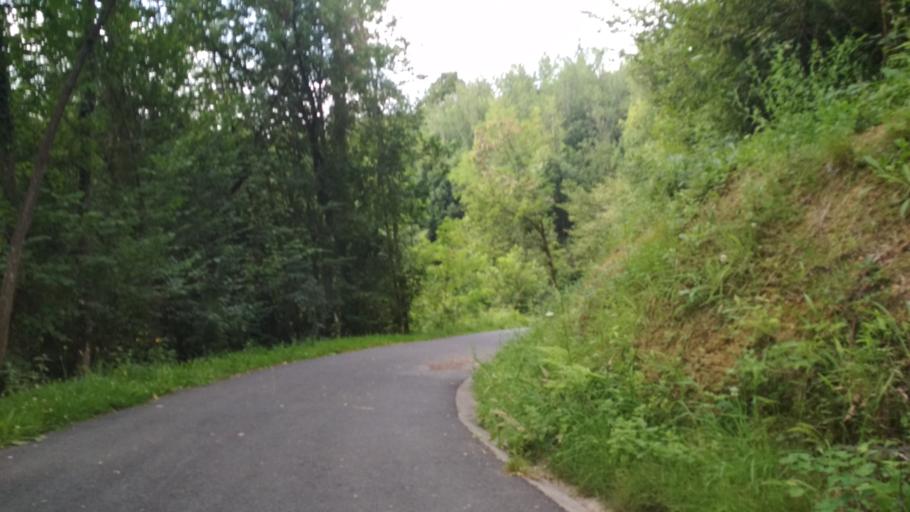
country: ES
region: Basque Country
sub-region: Provincia de Guipuzcoa
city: San Sebastian
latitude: 43.2970
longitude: -1.9835
